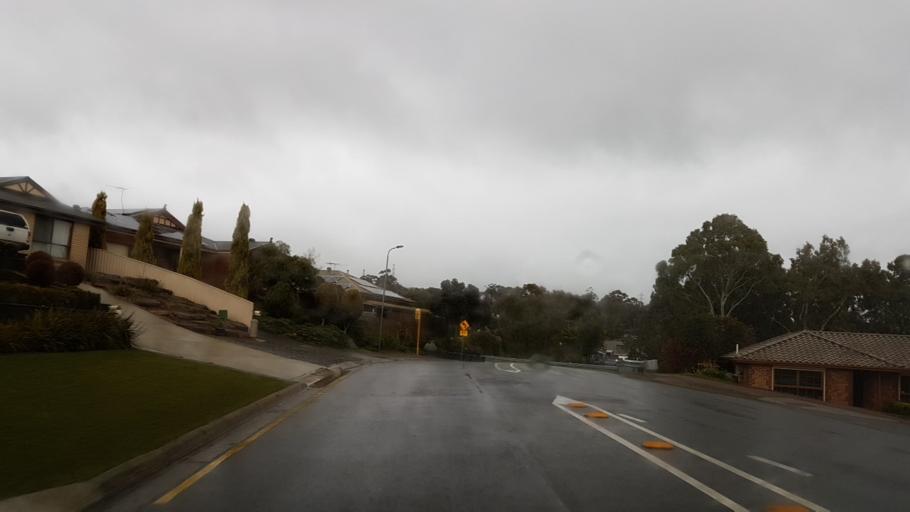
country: AU
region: South Australia
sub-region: Onkaparinga
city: Craigburn Farm
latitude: -35.0876
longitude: 138.5889
